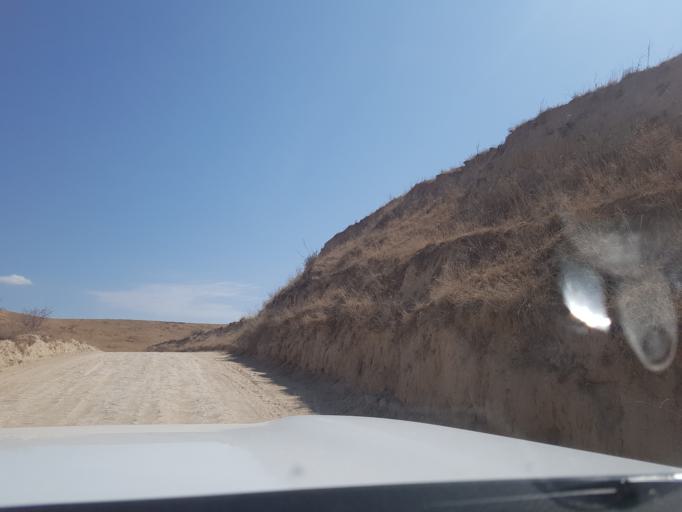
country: TM
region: Ahal
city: Baharly
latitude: 38.2745
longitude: 56.9005
